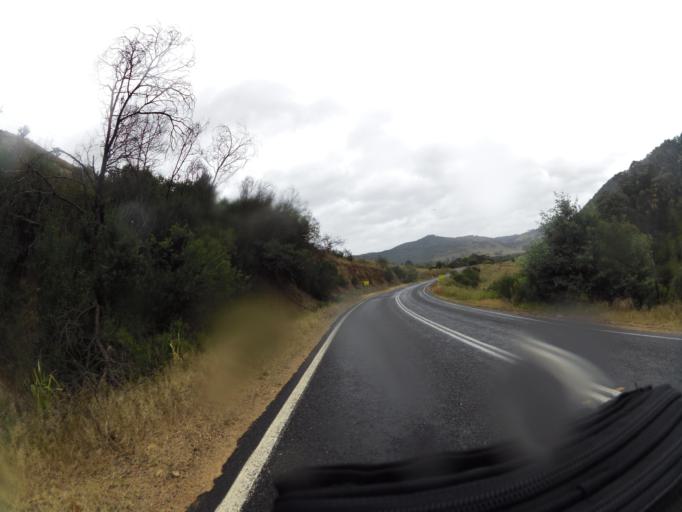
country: AU
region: New South Wales
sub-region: Greater Hume Shire
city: Holbrook
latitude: -36.2239
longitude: 147.6668
